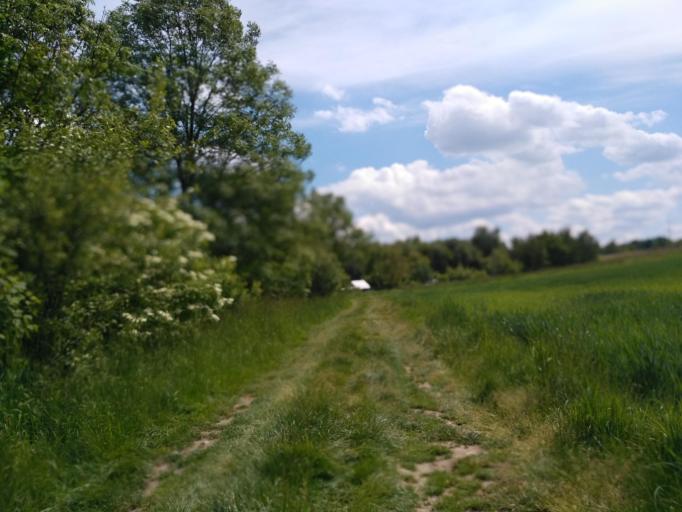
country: PL
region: Subcarpathian Voivodeship
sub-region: Powiat krosnienski
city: Odrzykon
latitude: 49.7159
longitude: 21.7528
